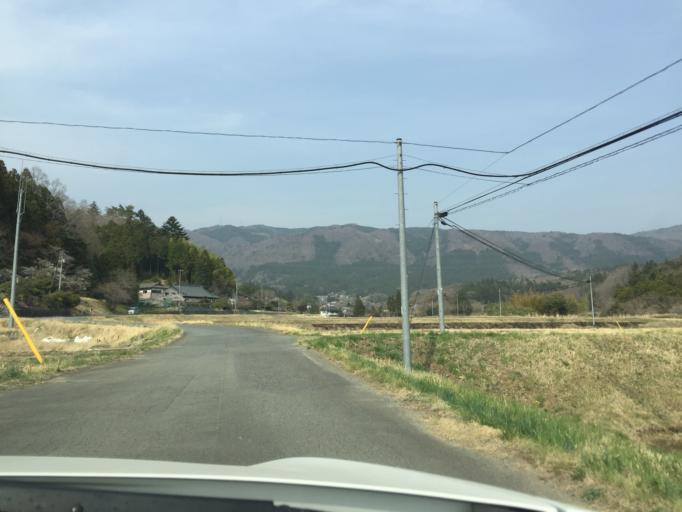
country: JP
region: Fukushima
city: Iwaki
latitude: 37.0256
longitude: 140.7329
